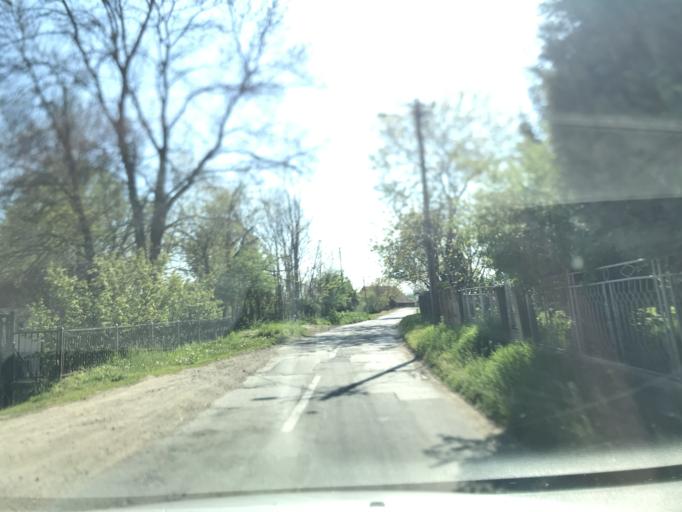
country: RS
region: Central Serbia
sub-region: Nisavski Okrug
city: Nis
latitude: 43.4102
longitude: 21.8160
